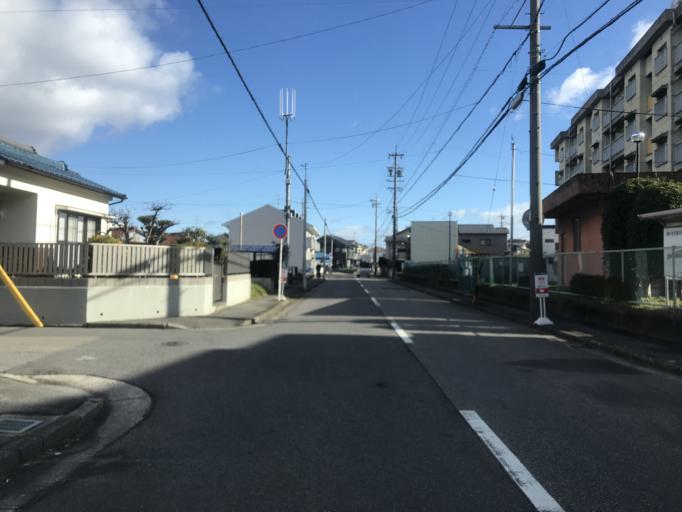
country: JP
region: Aichi
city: Nagoya-shi
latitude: 35.2047
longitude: 136.8470
